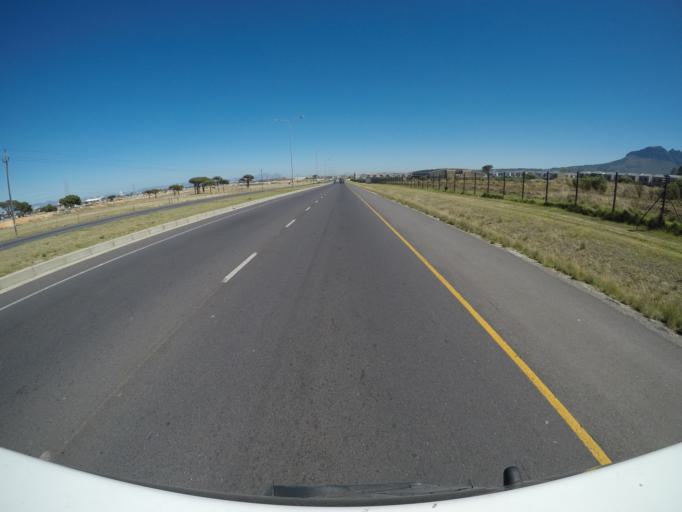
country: ZA
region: Western Cape
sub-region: Overberg District Municipality
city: Grabouw
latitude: -34.1111
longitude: 18.8659
